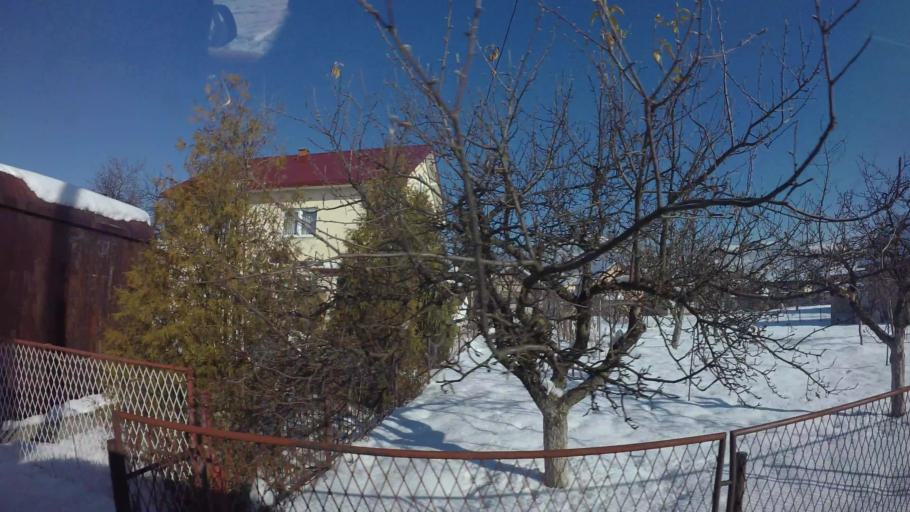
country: BA
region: Federation of Bosnia and Herzegovina
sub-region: Kanton Sarajevo
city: Sarajevo
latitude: 43.7991
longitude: 18.3452
